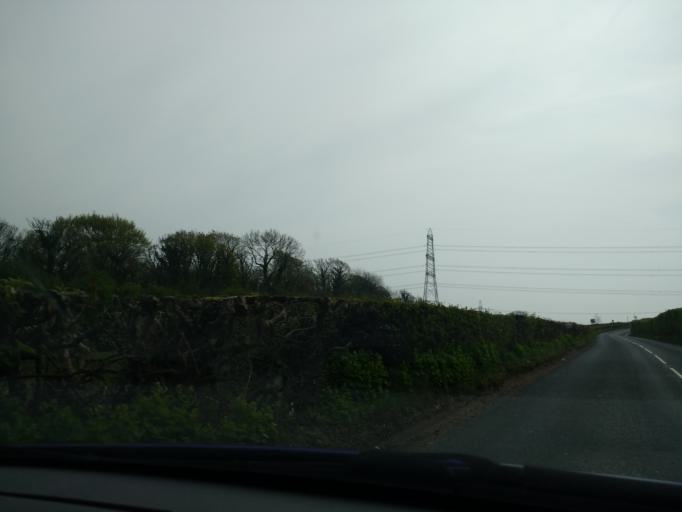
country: GB
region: England
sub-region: Lancashire
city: Lancaster
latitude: 54.0218
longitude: -2.8096
